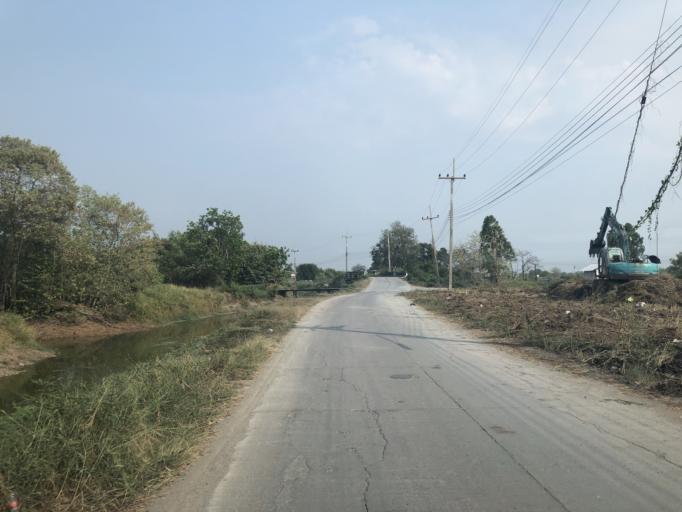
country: TH
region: Chachoengsao
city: Bang Pakong
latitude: 13.5096
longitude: 100.9350
